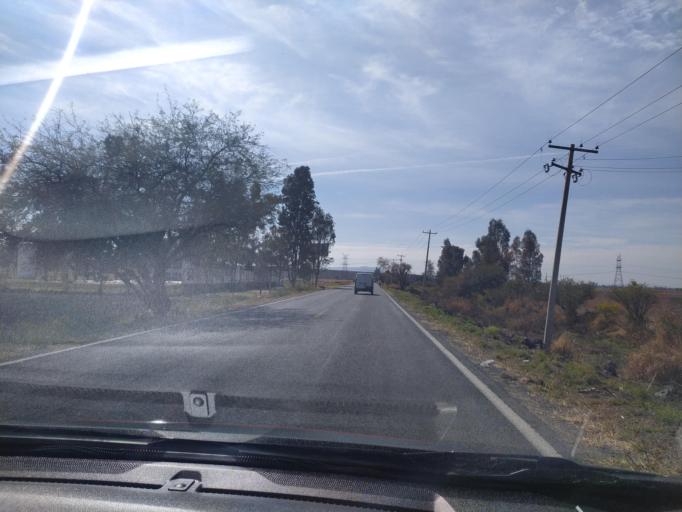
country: MX
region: Guanajuato
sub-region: San Francisco del Rincon
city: San Ignacio de Hidalgo
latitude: 20.9392
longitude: -101.8549
